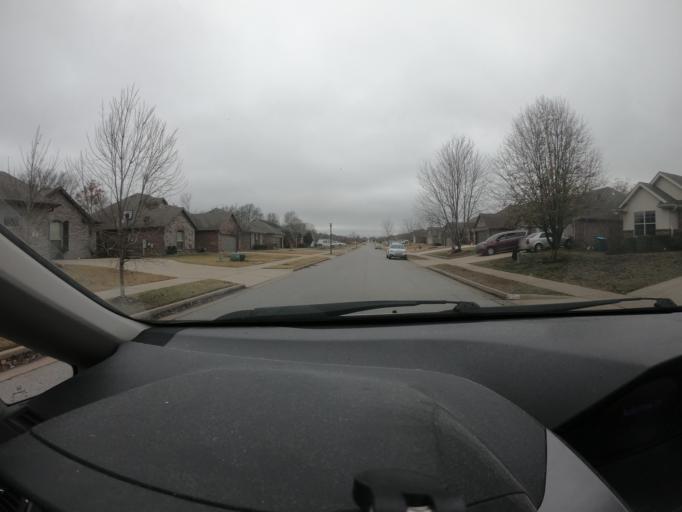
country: US
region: Arkansas
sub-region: Benton County
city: Centerton
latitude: 36.3405
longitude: -94.2457
